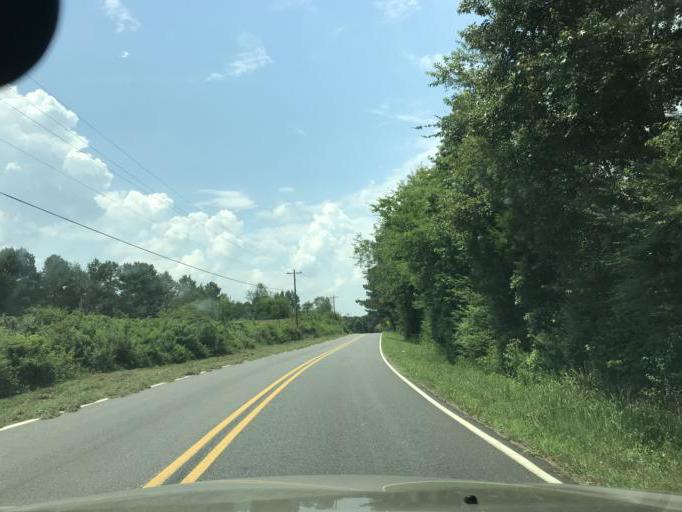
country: US
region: Georgia
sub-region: Dawson County
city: Dawsonville
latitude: 34.3230
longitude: -84.1624
